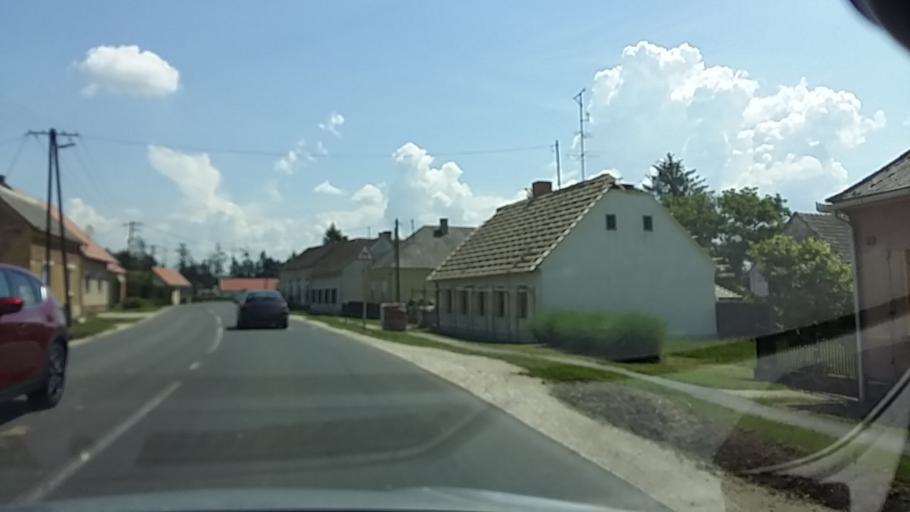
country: AT
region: Burgenland
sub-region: Politischer Bezirk Gussing
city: Heiligenbrunn
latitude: 46.9697
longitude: 16.4114
